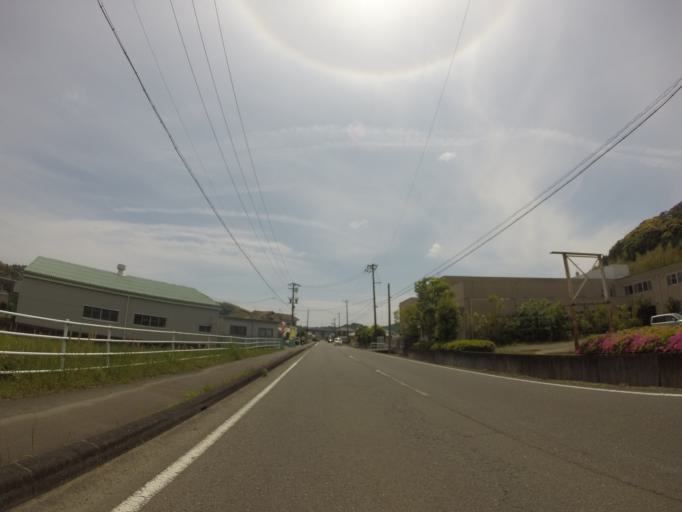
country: JP
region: Shizuoka
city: Fujieda
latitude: 34.9091
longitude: 138.2468
